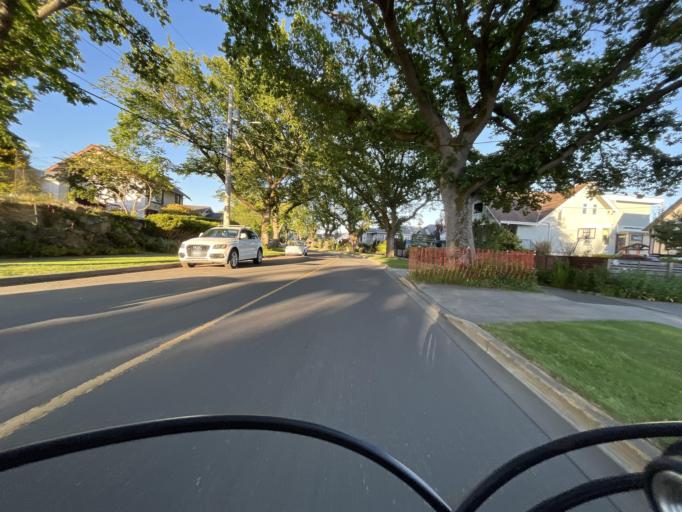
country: CA
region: British Columbia
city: Victoria
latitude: 48.4087
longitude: -123.3327
